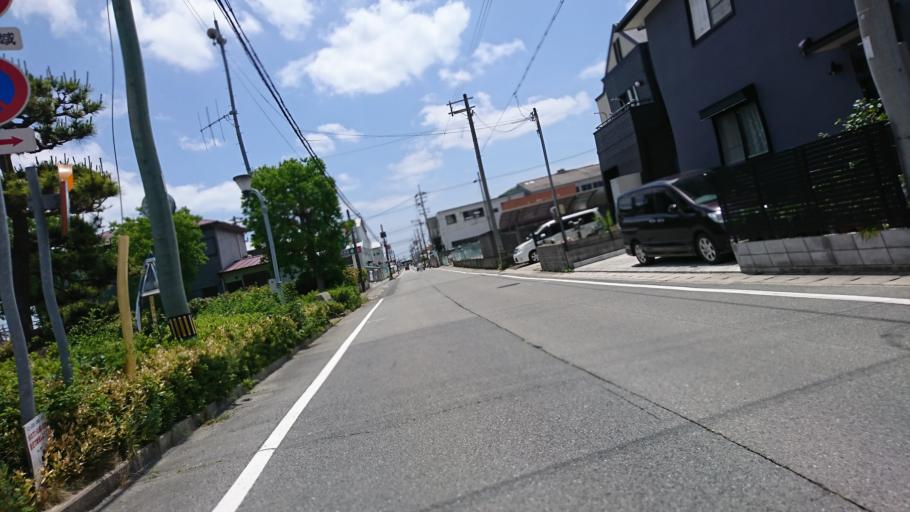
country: JP
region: Hyogo
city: Shirahamacho-usazakiminami
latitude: 34.7894
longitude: 134.7509
